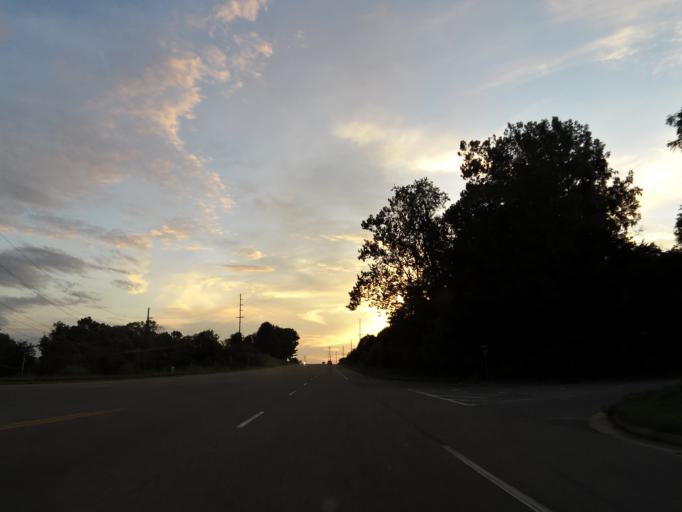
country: US
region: Tennessee
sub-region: Carter County
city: Elizabethton
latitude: 36.3603
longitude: -82.1952
